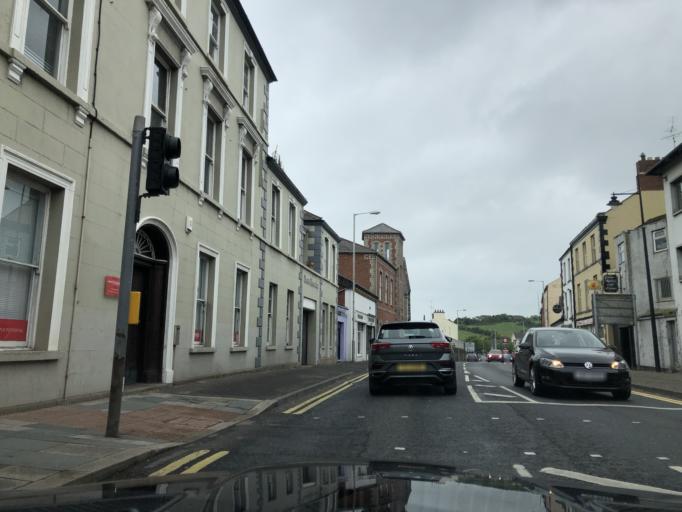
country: GB
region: Northern Ireland
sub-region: Down District
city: Downpatrick
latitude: 54.3289
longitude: -5.7159
